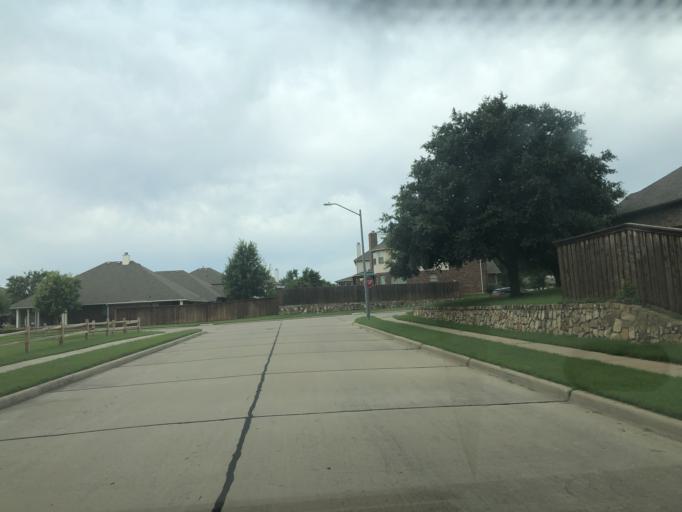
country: US
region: Texas
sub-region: Dallas County
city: Irving
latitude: 32.7951
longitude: -96.9858
